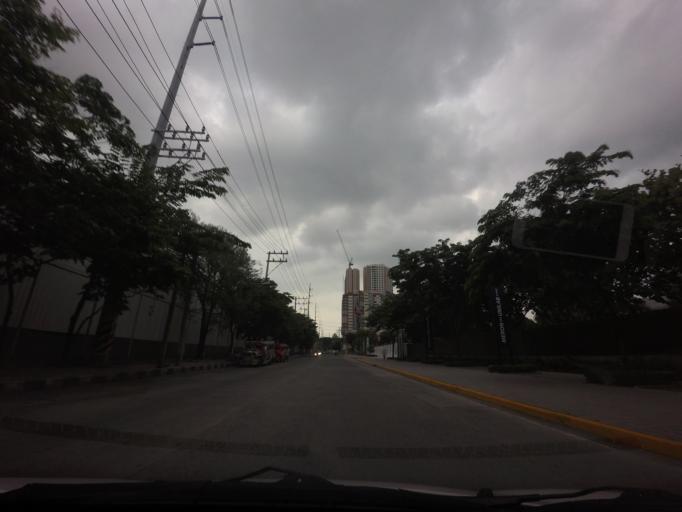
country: PH
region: Metro Manila
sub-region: Pasig
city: Pasig City
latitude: 14.5755
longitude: 121.0569
